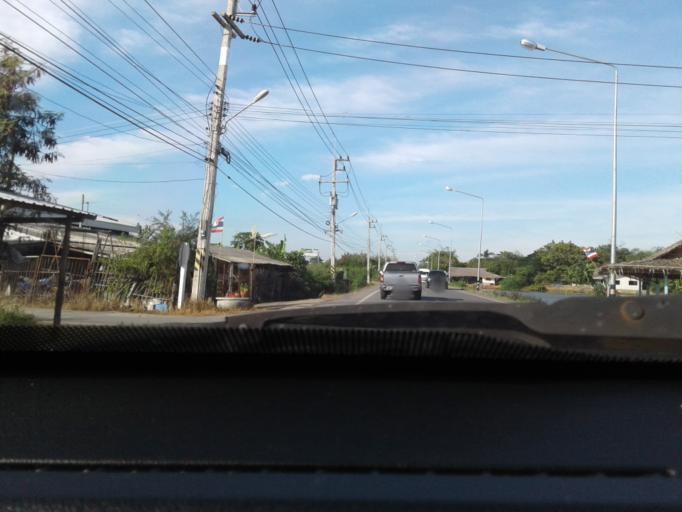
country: TH
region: Nakhon Pathom
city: Bang Len
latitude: 13.9664
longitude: 100.2041
